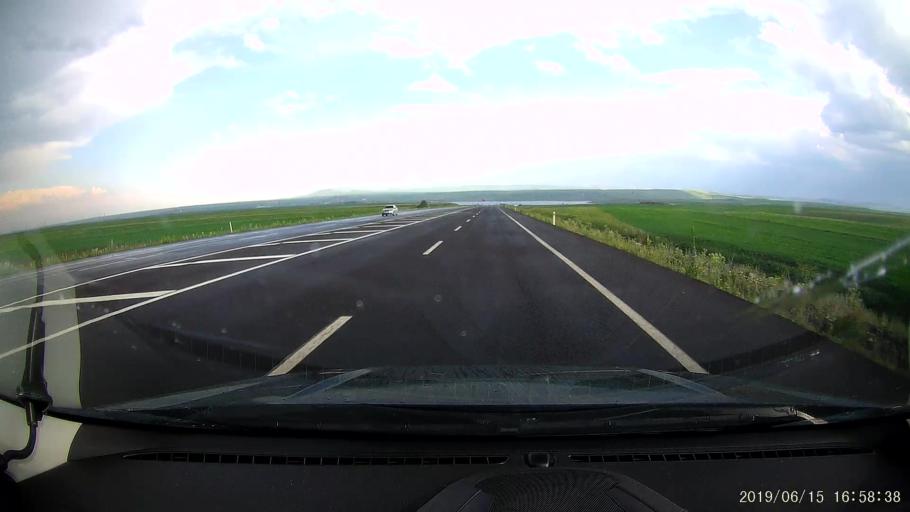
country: TR
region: Kars
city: Susuz
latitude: 40.7624
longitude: 43.1449
